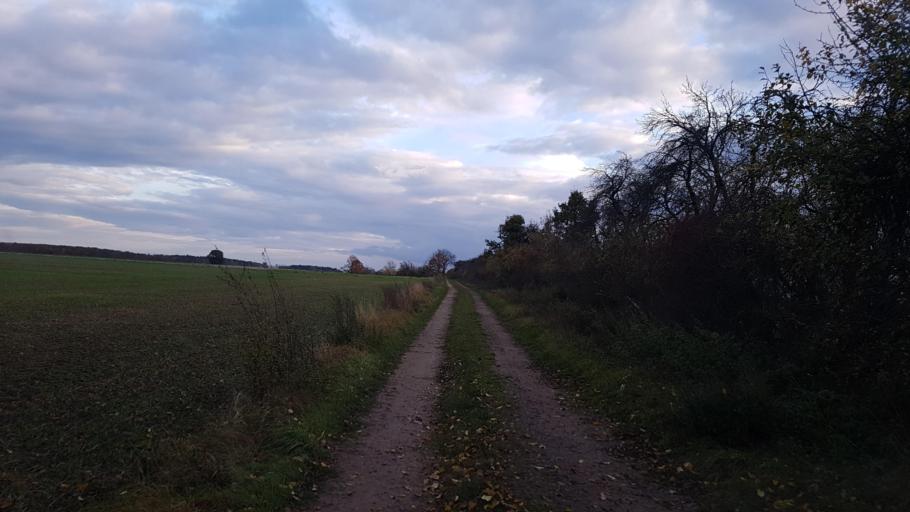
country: DE
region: Saxony-Anhalt
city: Seyda
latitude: 51.9439
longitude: 12.8712
